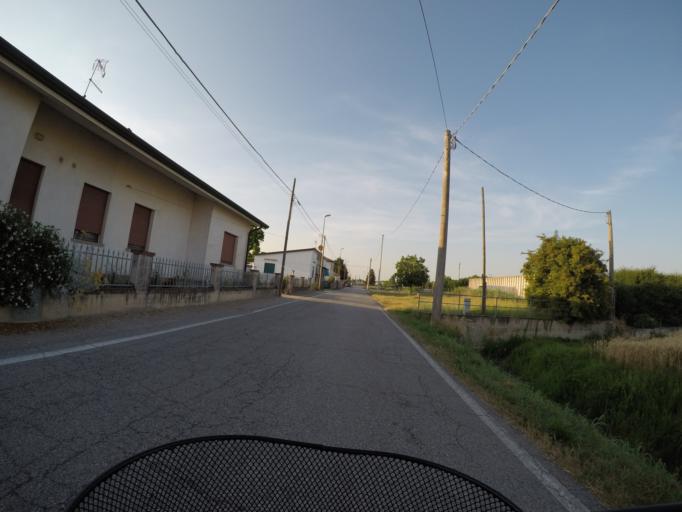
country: IT
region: Veneto
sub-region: Provincia di Rovigo
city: San Bellino
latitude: 45.0222
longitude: 11.5867
